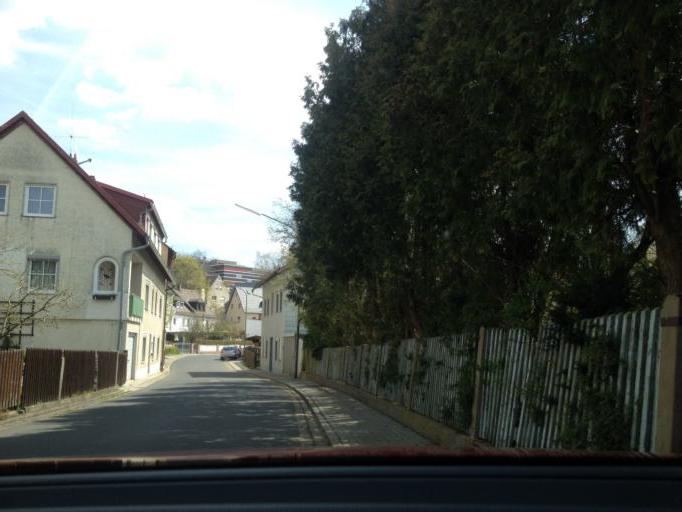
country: DE
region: Bavaria
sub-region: Upper Franconia
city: Arzberg
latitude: 50.0598
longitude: 12.1830
